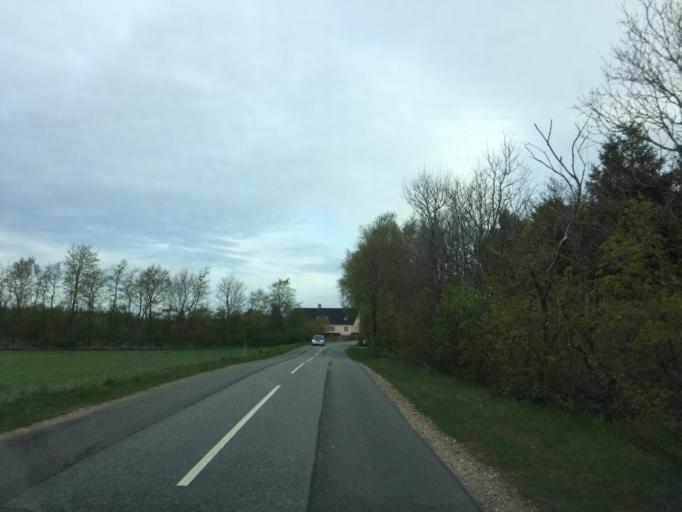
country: DK
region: Central Jutland
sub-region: Viborg Kommune
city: Karup
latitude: 56.3417
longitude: 9.0818
